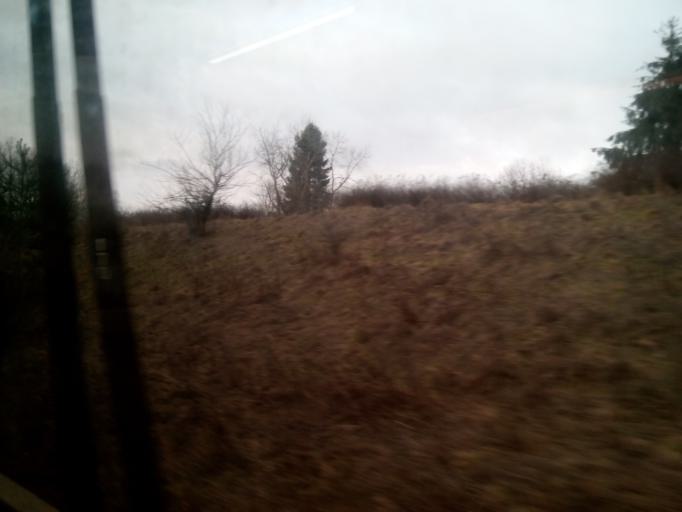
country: SK
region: Zilinsky
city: Ruzomberok
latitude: 49.0880
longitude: 19.4515
